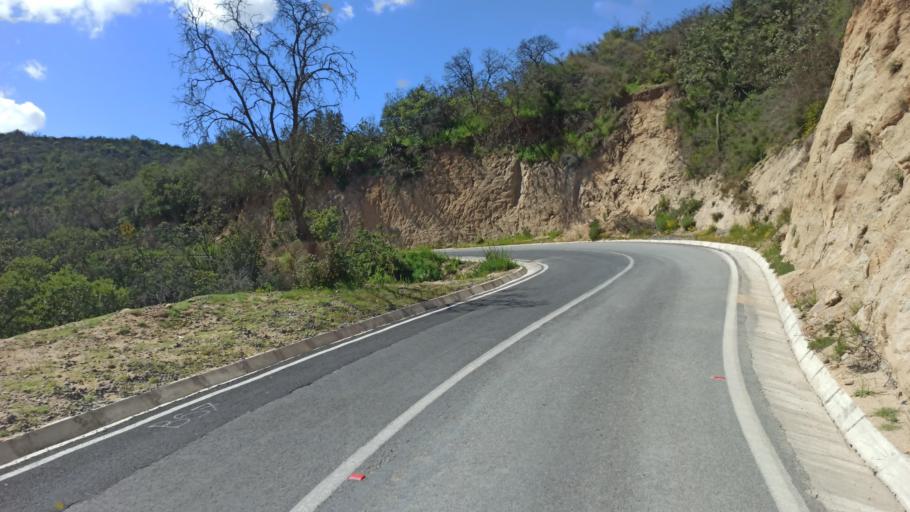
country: CL
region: Valparaiso
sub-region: Provincia de Marga Marga
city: Limache
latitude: -33.2063
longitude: -71.2566
